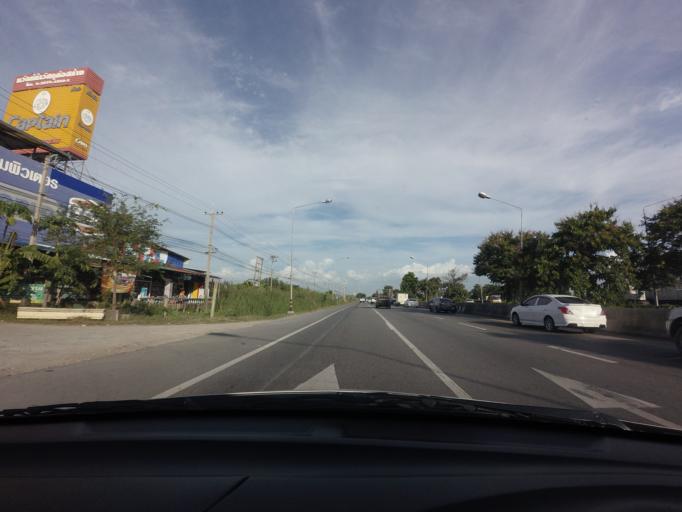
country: TH
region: Pathum Thani
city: Lat Lum Kaeo
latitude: 14.0179
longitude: 100.3610
